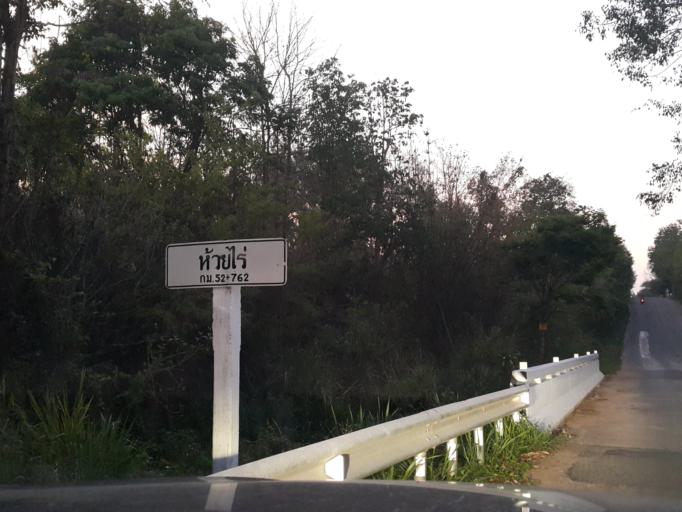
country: TH
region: Lamphun
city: Thung Hua Chang
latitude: 18.0484
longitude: 99.0245
